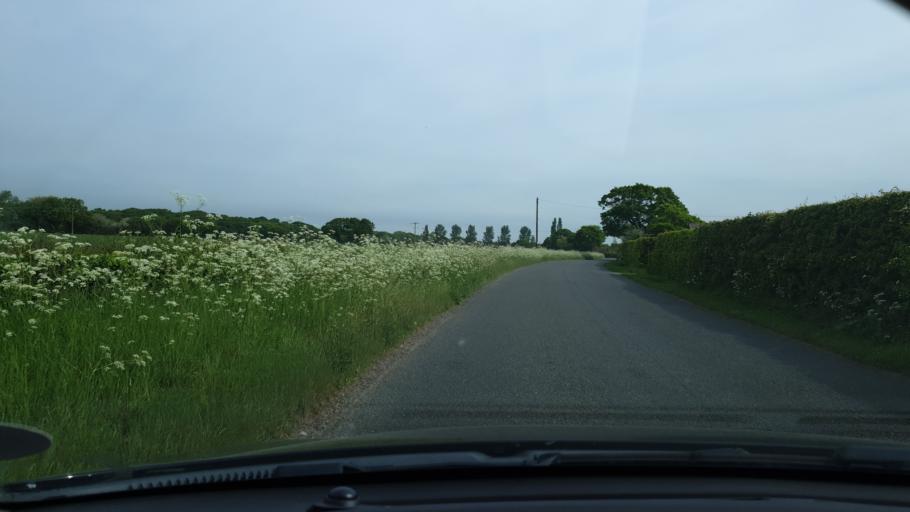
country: GB
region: England
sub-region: Essex
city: Little Clacton
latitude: 51.8239
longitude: 1.1111
